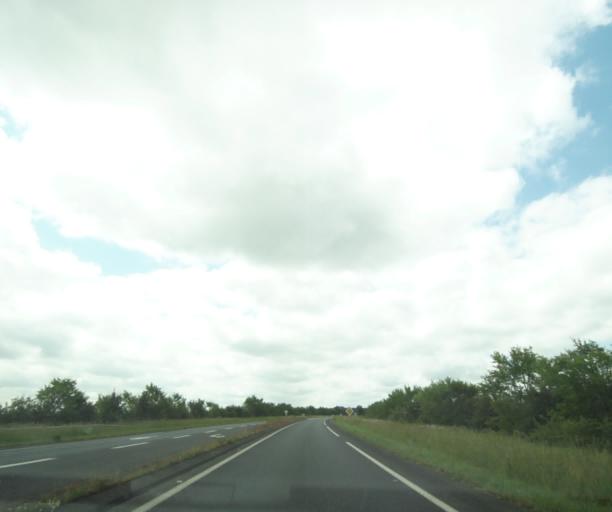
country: FR
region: Poitou-Charentes
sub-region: Departement des Deux-Sevres
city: Saint-Varent
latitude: 46.8756
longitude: -0.1967
